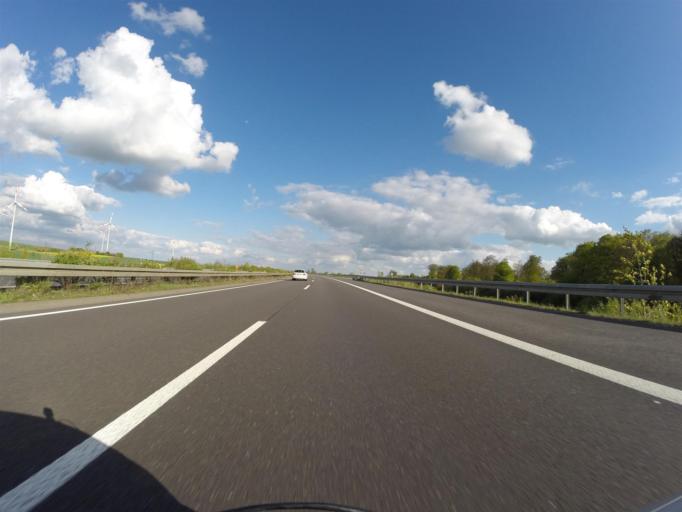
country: DE
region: Saarland
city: Orscholz
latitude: 49.4557
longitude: 6.4812
